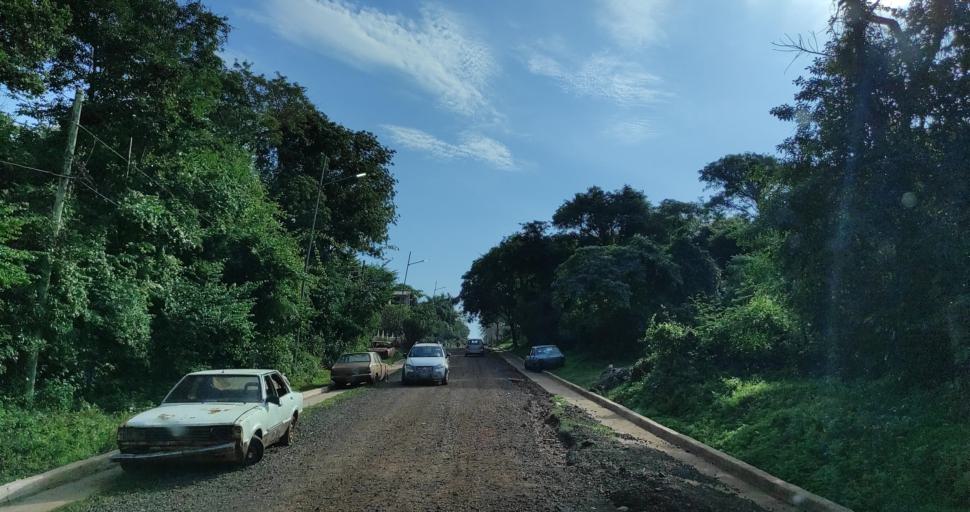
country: AR
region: Corrientes
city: Santo Tome
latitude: -28.5532
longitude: -56.0278
